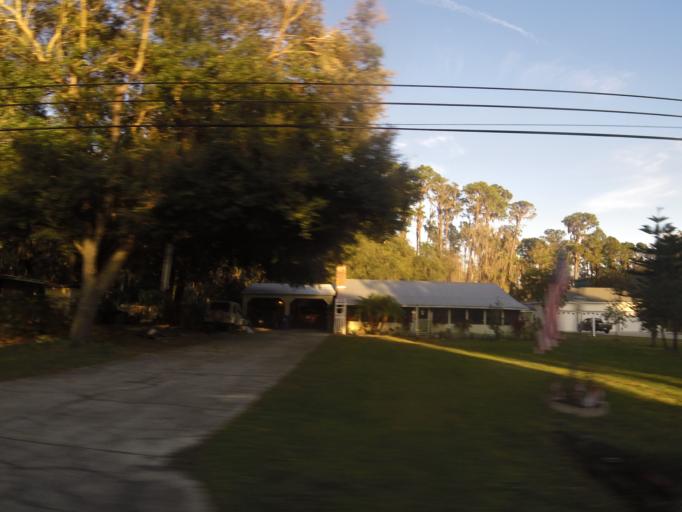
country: US
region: Florida
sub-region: Putnam County
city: East Palatka
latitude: 29.8200
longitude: -81.5513
